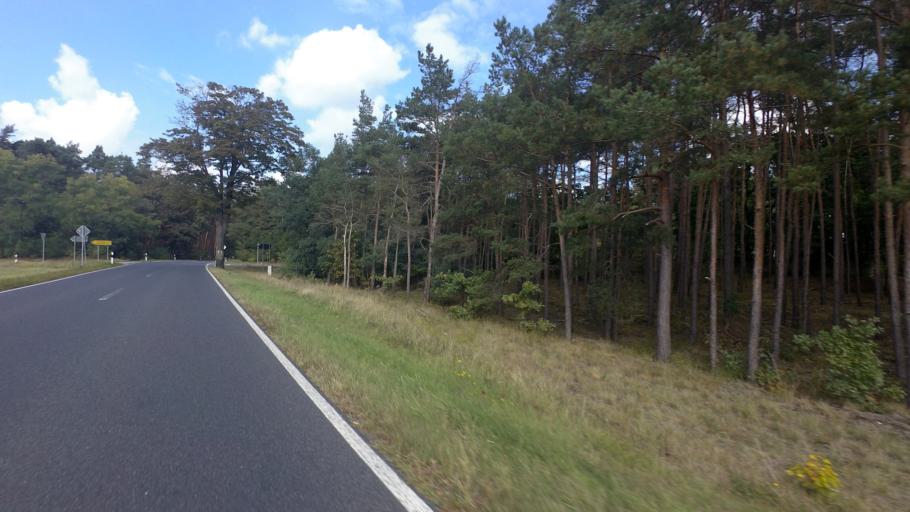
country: DE
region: Saxony-Anhalt
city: Holzdorf
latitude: 51.8389
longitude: 13.1443
